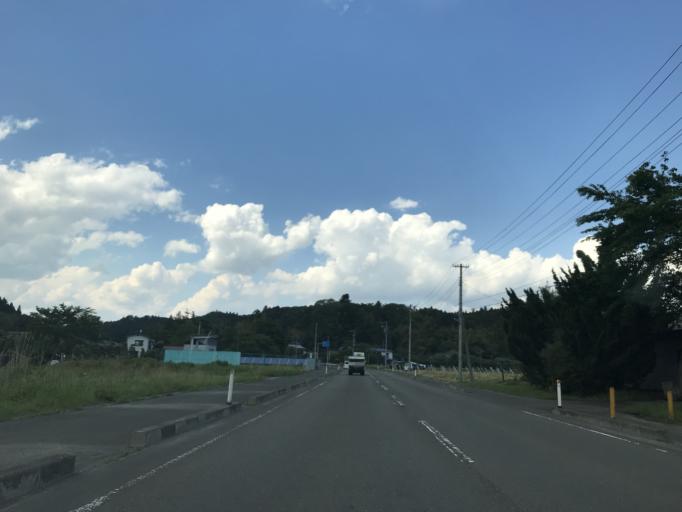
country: JP
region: Miyagi
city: Wakuya
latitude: 38.5478
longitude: 141.1412
